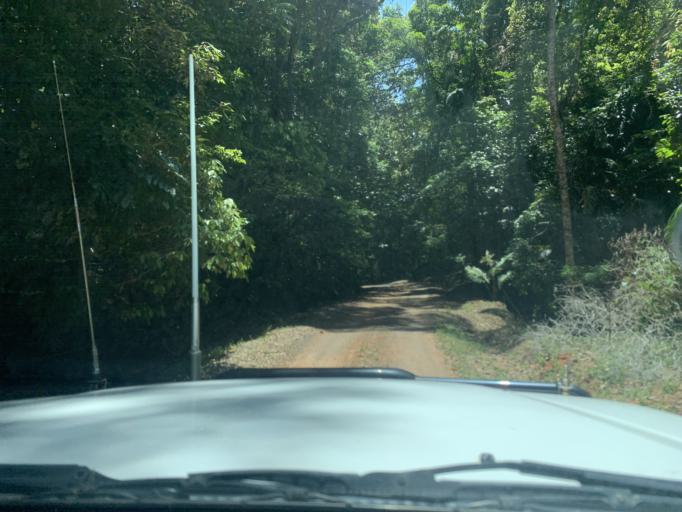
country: AU
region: Queensland
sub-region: Cairns
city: Redlynch
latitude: -16.9589
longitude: 145.6437
